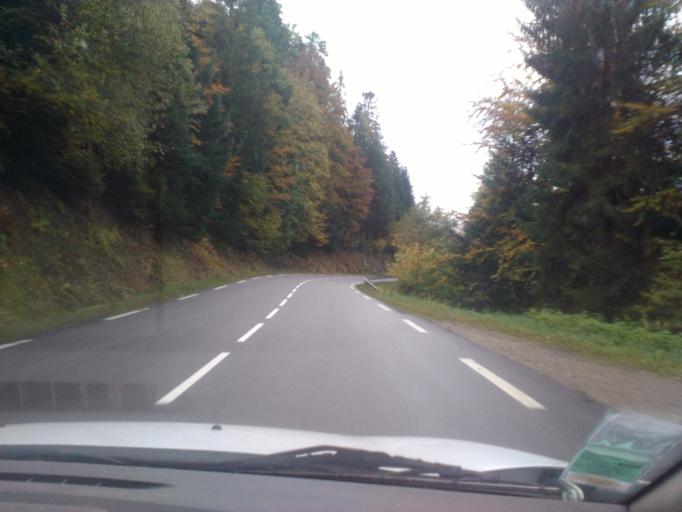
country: FR
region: Lorraine
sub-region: Departement des Vosges
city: Xonrupt-Longemer
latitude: 48.1121
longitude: 6.9104
